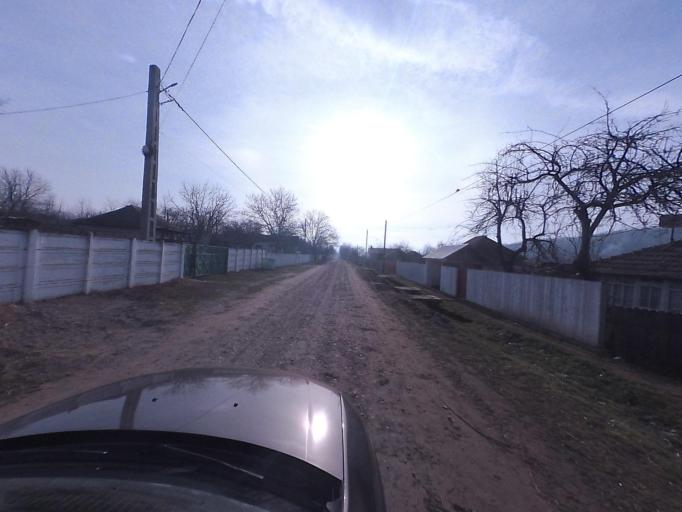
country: RO
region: Vaslui
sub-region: Comuna Solesti
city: Solesti
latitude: 46.8077
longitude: 27.7787
